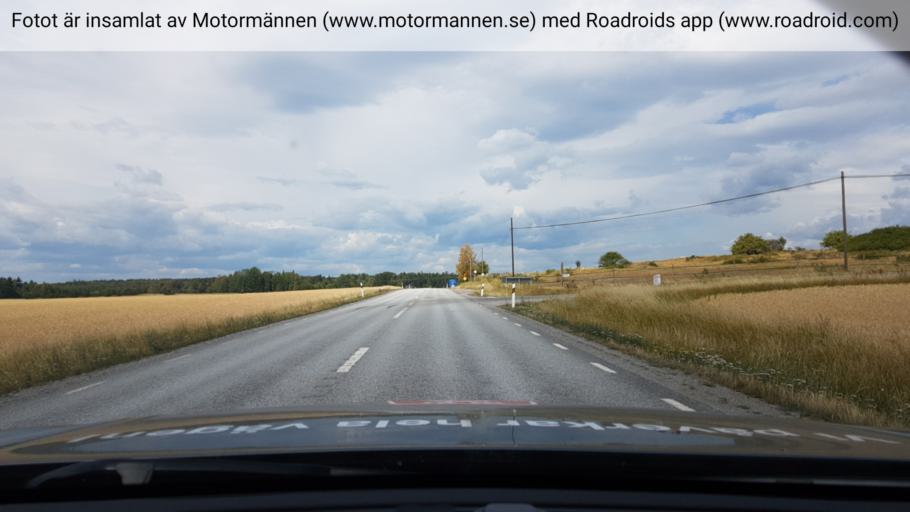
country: SE
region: Uppsala
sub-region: Habo Kommun
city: Balsta
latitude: 59.6246
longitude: 17.6037
